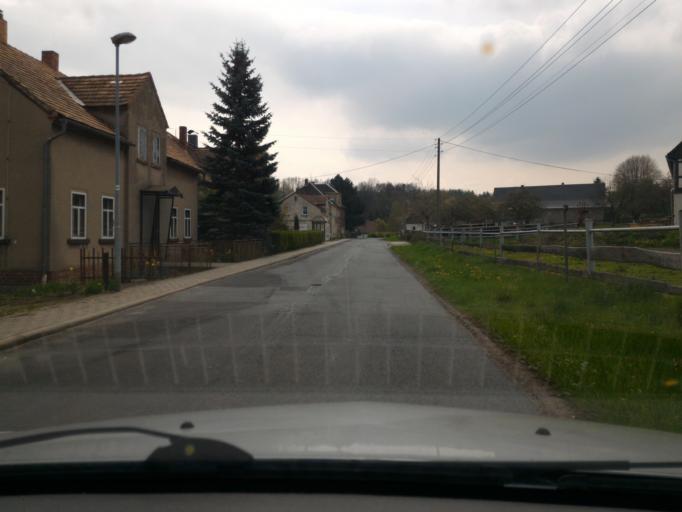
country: DE
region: Saxony
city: Grossschonau
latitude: 50.9010
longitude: 14.6927
